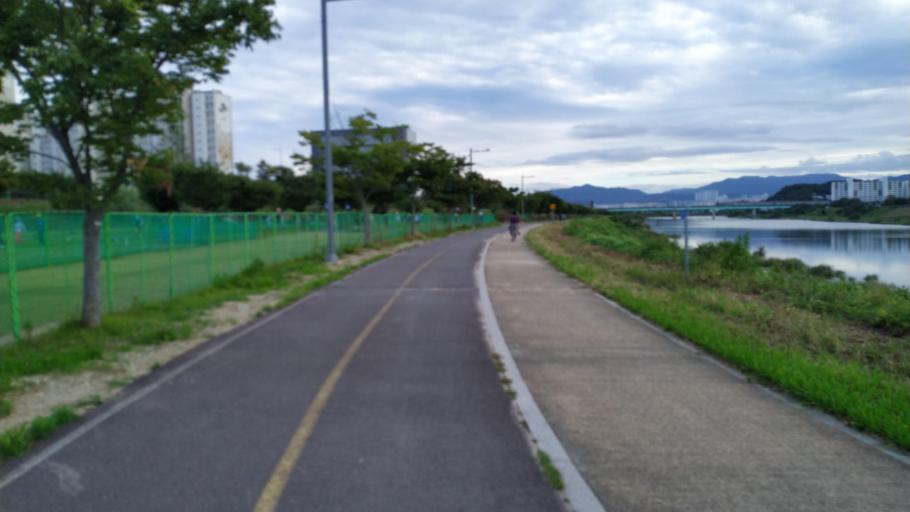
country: KR
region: Daegu
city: Daegu
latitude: 35.9264
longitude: 128.6322
